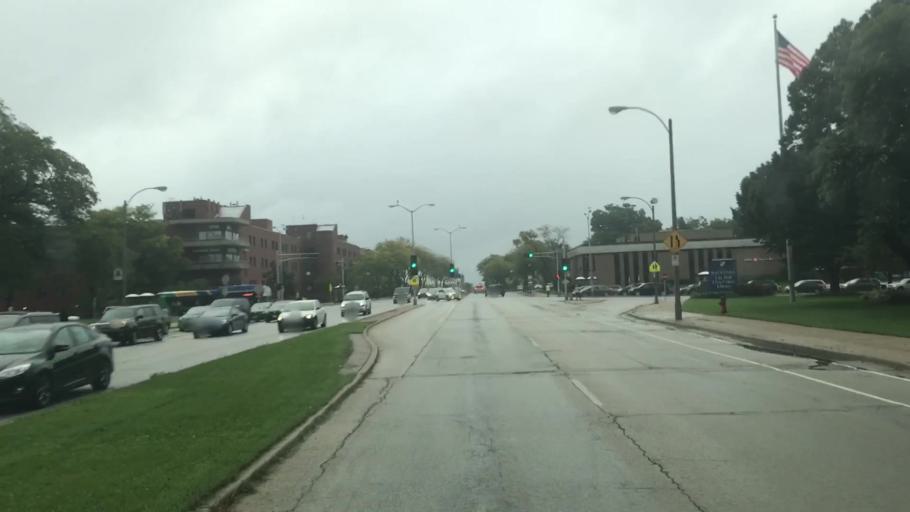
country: US
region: Wisconsin
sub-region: Milwaukee County
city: Wauwatosa
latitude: 43.0607
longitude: -88.0088
